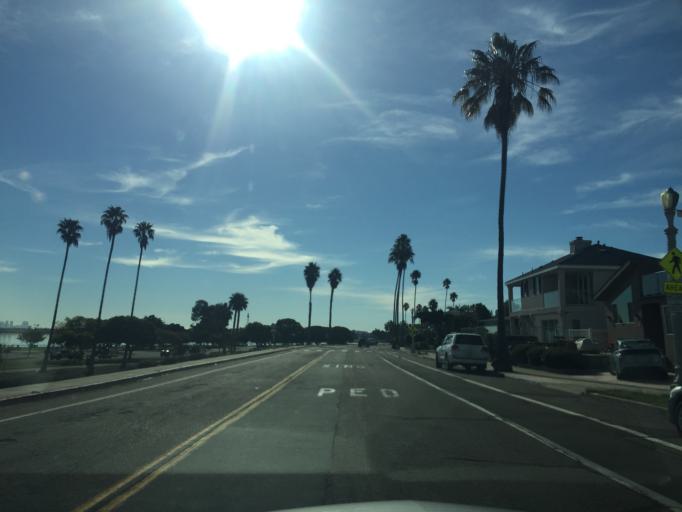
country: US
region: California
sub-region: San Diego County
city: La Jolla
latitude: 32.7857
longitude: -117.2342
